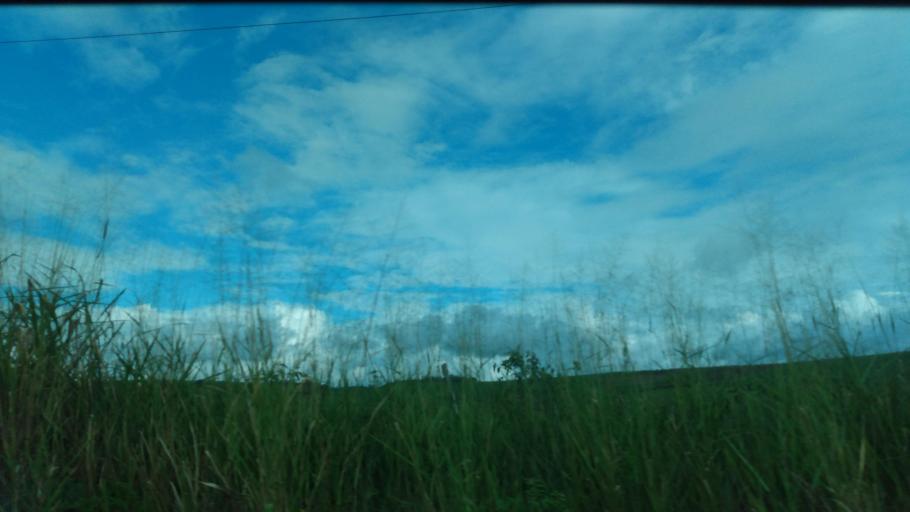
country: BR
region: Pernambuco
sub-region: Catende
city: Catende
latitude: -8.6992
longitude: -35.7384
